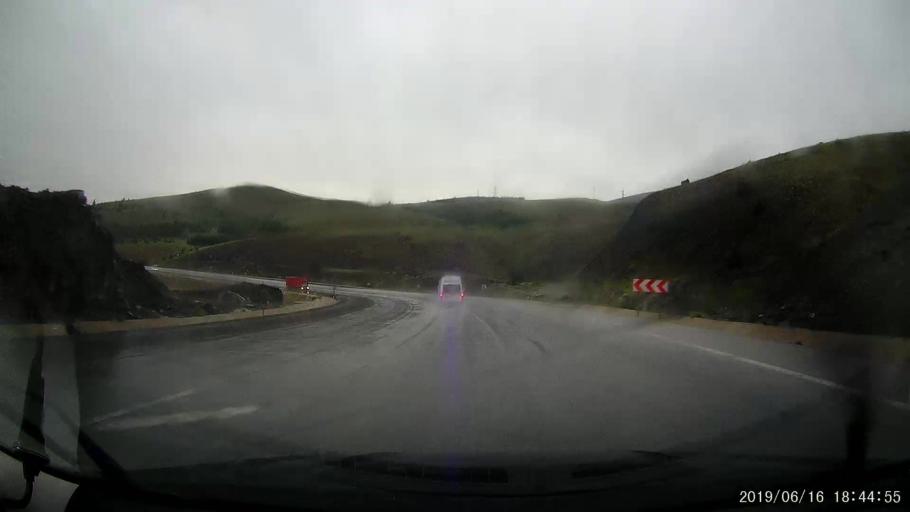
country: TR
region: Erzincan
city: Doganbeyli
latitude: 39.8713
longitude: 39.0657
